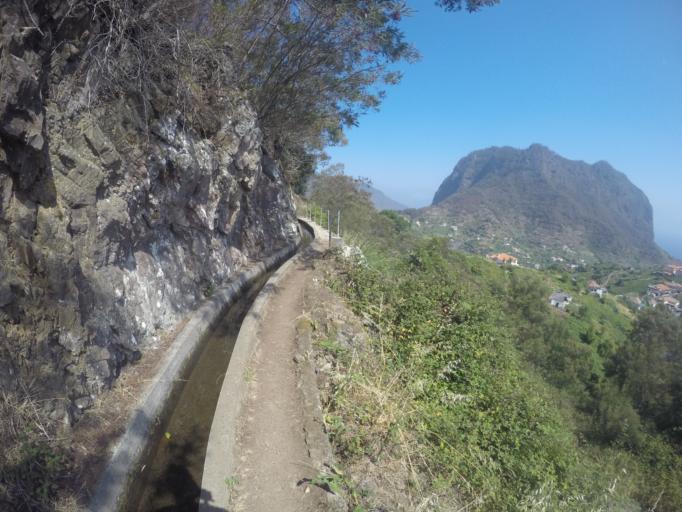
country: PT
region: Madeira
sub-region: Santana
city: Santana
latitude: 32.7554
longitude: -16.8395
